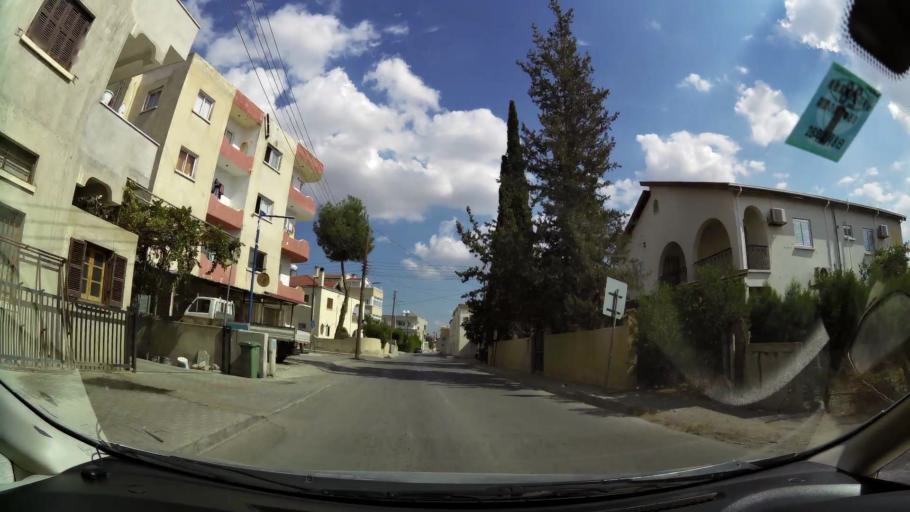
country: CY
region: Lefkosia
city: Nicosia
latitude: 35.2160
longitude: 33.3023
